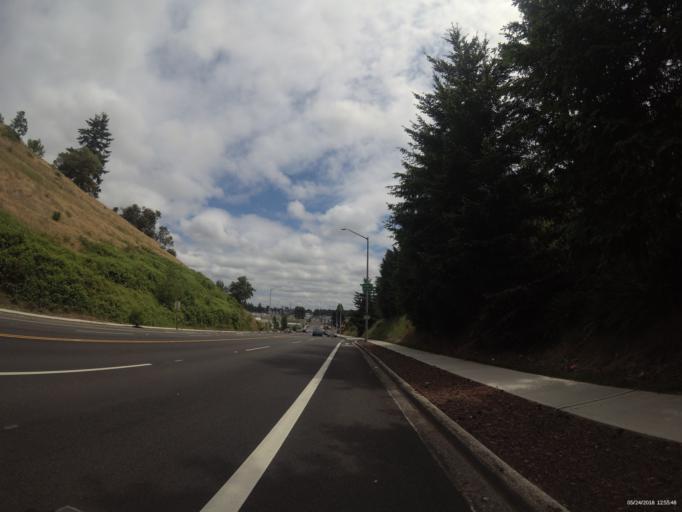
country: US
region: Washington
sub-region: Pierce County
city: Fircrest
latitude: 47.2062
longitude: -122.4949
